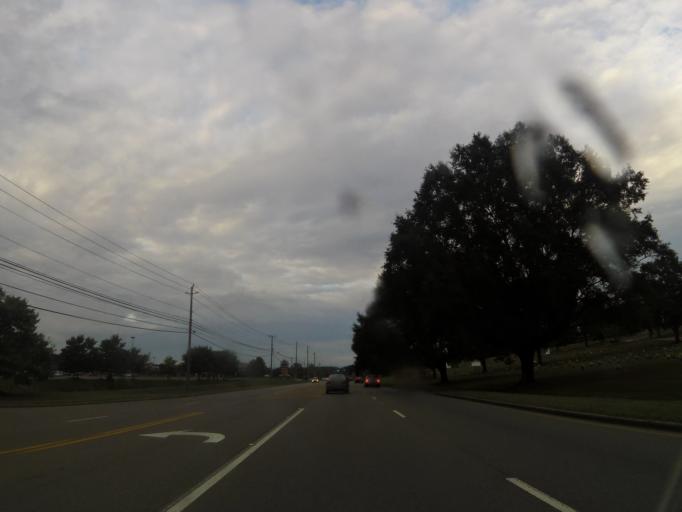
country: US
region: Alabama
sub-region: Jefferson County
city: Trussville
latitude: 33.6025
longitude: -86.6375
